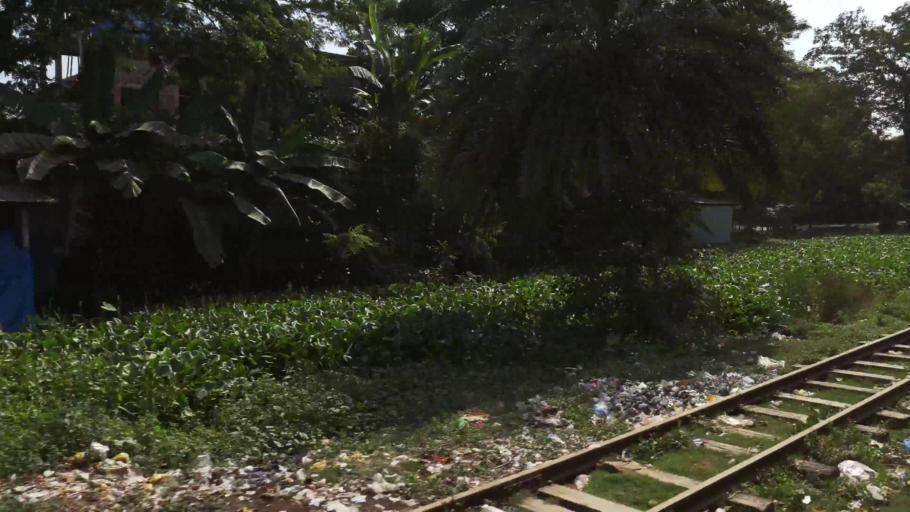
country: BD
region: Dhaka
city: Gafargaon
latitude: 24.1911
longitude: 90.4772
